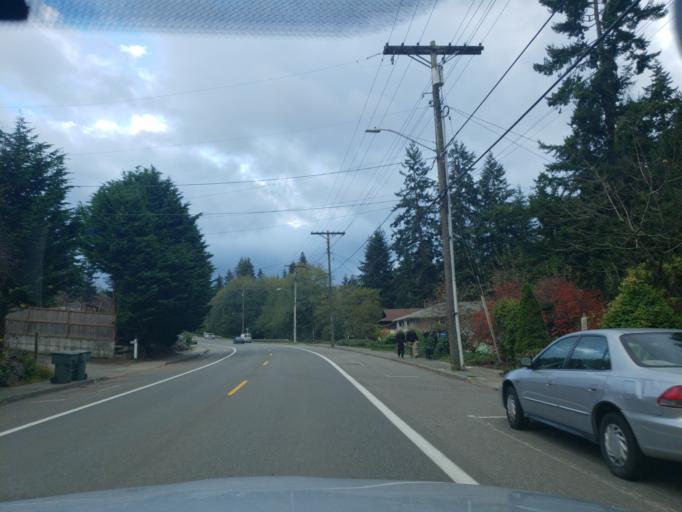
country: US
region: Washington
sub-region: Snohomish County
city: Everett
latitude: 47.9536
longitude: -122.2475
